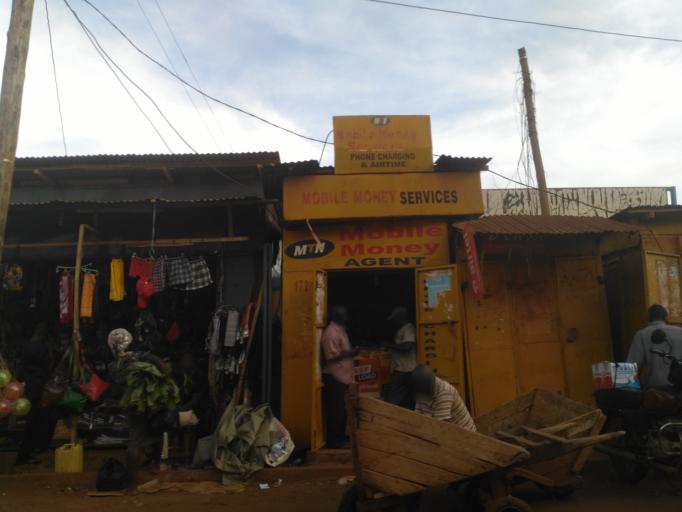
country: UG
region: Eastern Region
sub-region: Jinja District
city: Jinja
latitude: 0.4316
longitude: 33.2142
